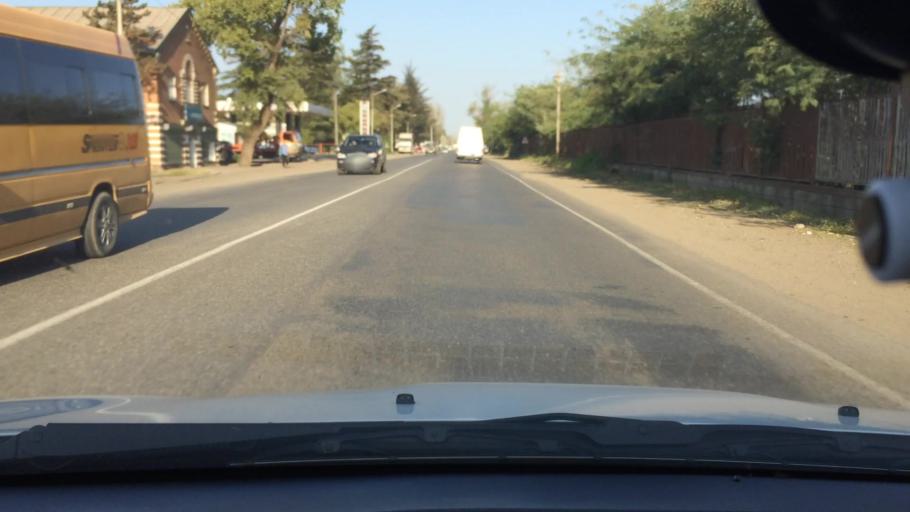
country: GE
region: Imereti
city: Zestap'oni
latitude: 42.1207
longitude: 43.0097
